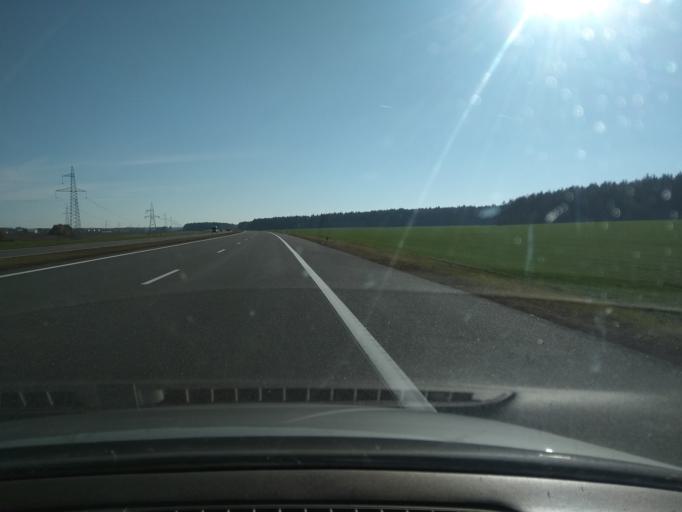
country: BY
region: Brest
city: Baranovichi
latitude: 53.0976
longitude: 25.8864
